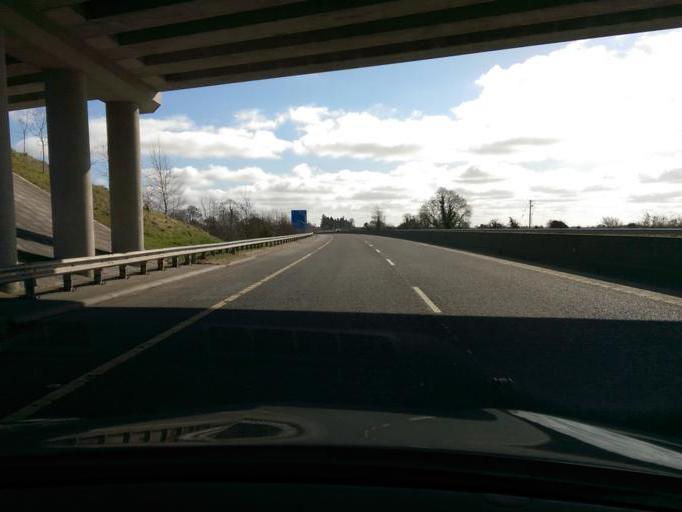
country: IE
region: Leinster
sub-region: An Iarmhi
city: Kilbeggan
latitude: 53.3625
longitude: -7.5211
